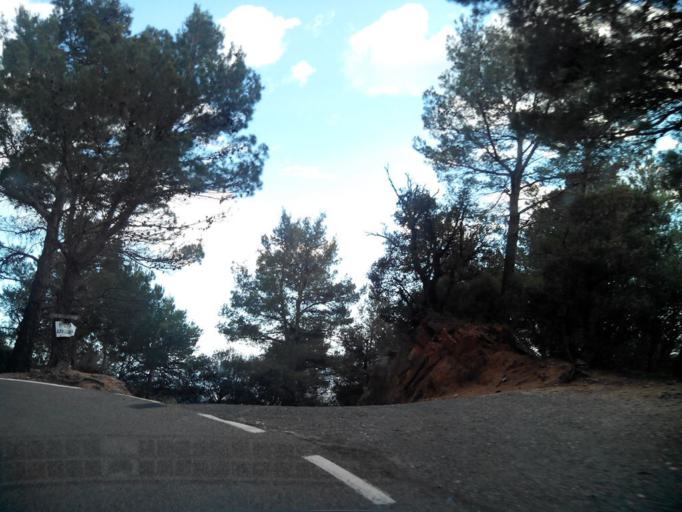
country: ES
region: Catalonia
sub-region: Provincia de Tarragona
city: Vilaplana
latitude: 41.2361
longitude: 1.0562
